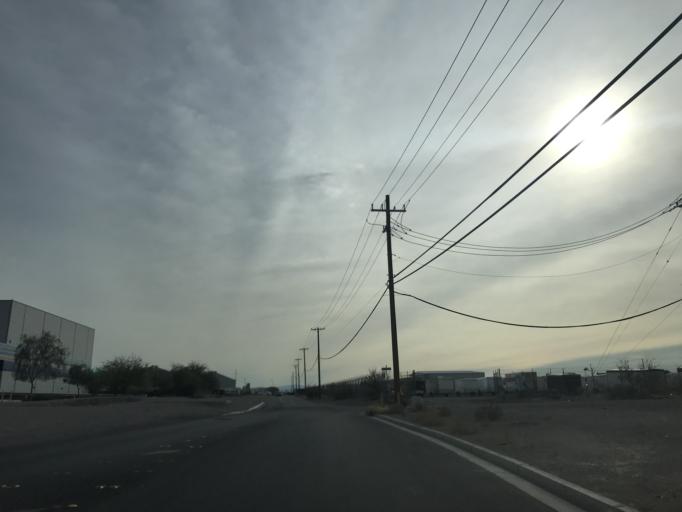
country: US
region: Nevada
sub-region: Clark County
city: Paradise
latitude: 36.0903
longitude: -115.1681
